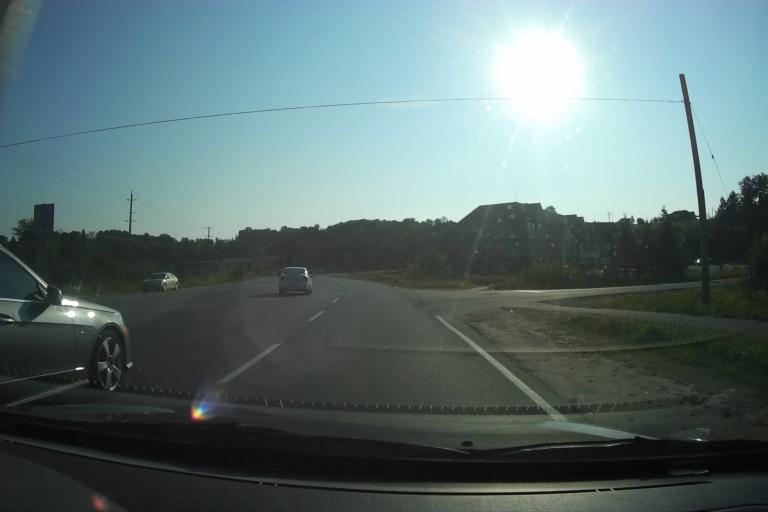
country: CA
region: Ontario
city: Huntsville
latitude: 45.3429
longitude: -79.2283
